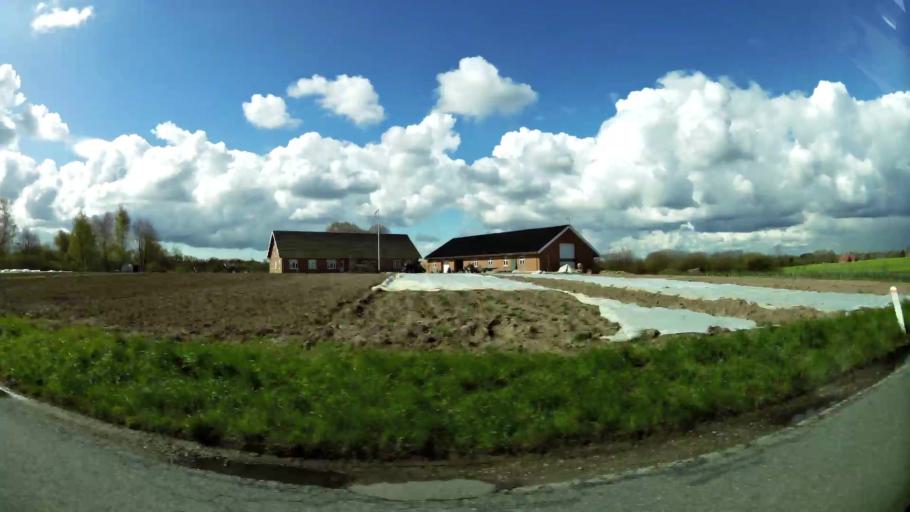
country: DK
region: South Denmark
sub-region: Middelfart Kommune
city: Brenderup
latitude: 55.4680
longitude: 10.0090
